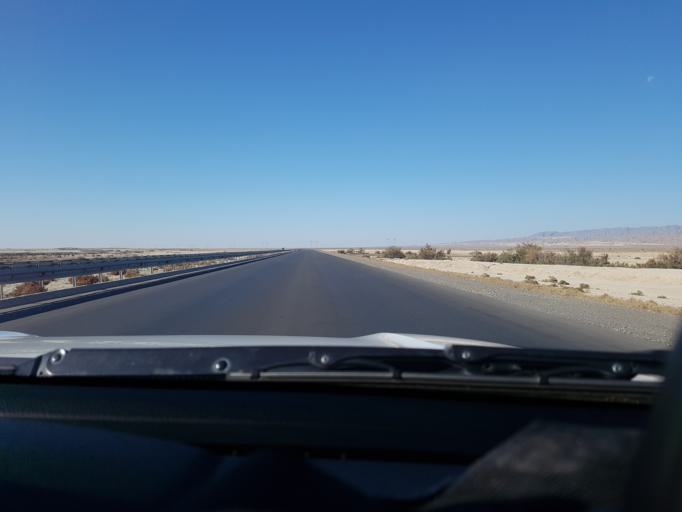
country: TM
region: Balkan
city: Gazanjyk
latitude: 39.2653
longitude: 55.1243
